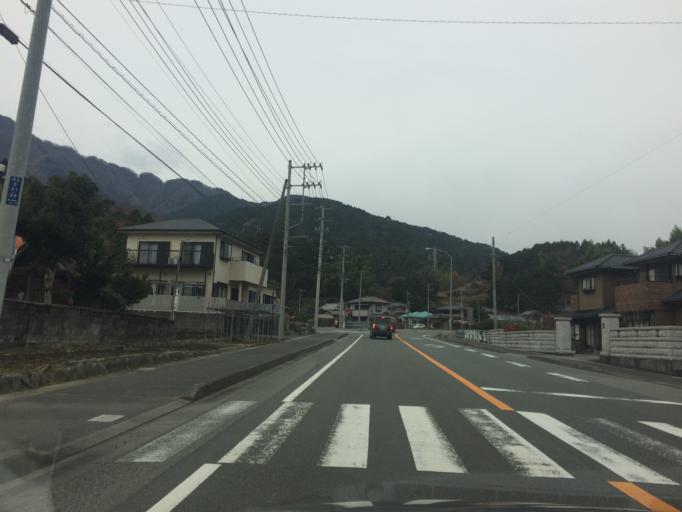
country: JP
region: Shizuoka
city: Fujinomiya
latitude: 35.2637
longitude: 138.4642
